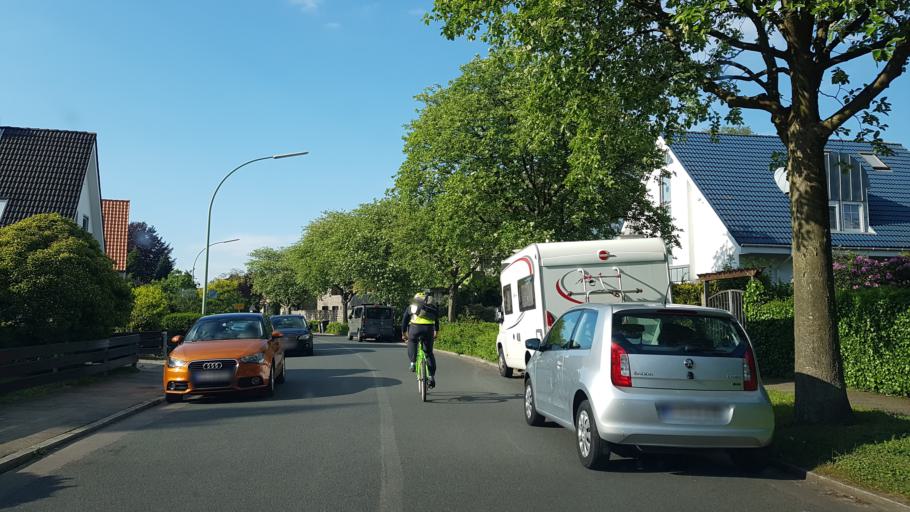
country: DE
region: Lower Saxony
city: Langen
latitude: 53.5923
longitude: 8.5934
